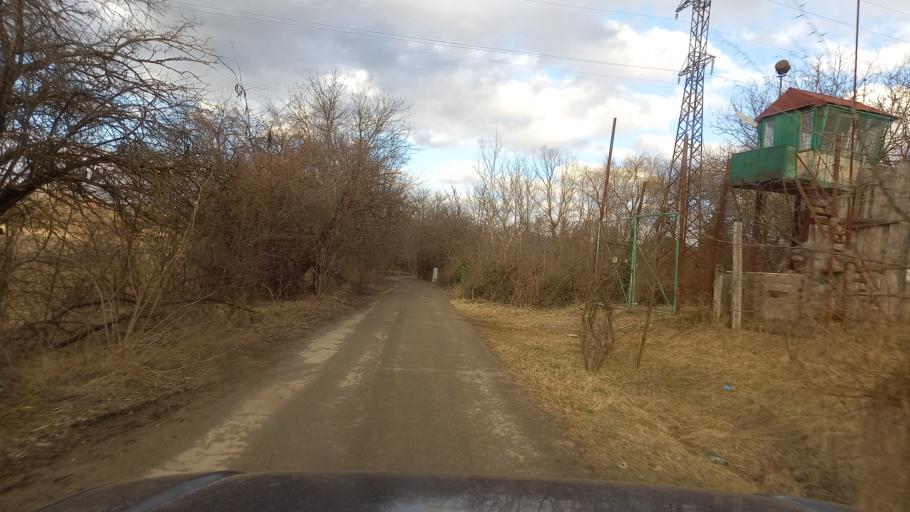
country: RU
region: Adygeya
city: Maykop
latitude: 44.5921
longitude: 40.0746
